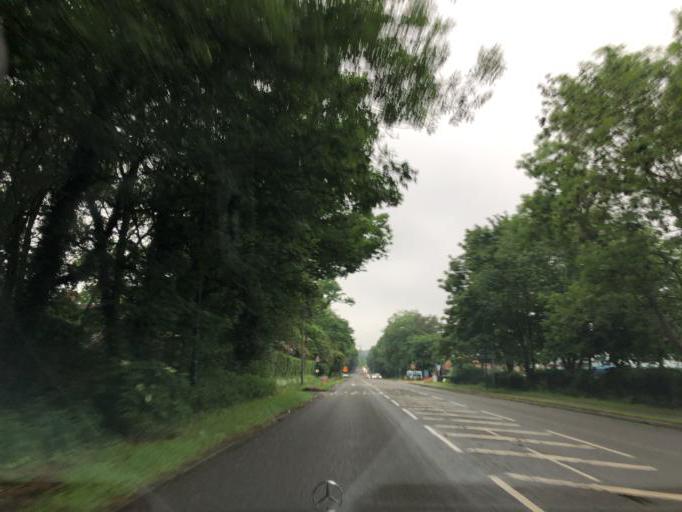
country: GB
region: England
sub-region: Warwickshire
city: Warwick
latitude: 52.2760
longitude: -1.5757
